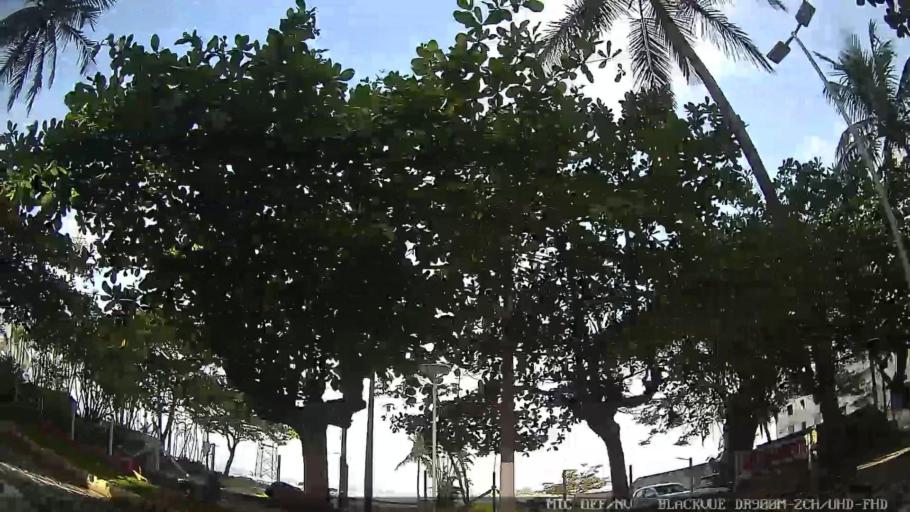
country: BR
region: Sao Paulo
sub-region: Guaruja
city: Guaruja
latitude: -23.9968
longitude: -46.2560
